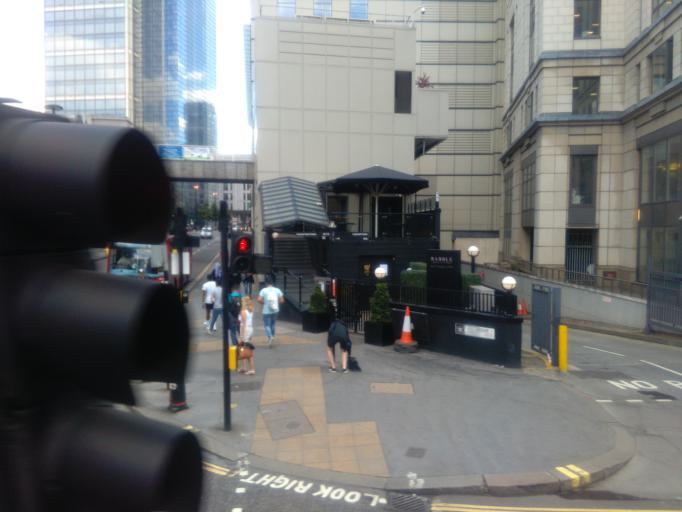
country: GB
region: England
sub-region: Greater London
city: City of London
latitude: 51.5151
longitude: -0.0853
